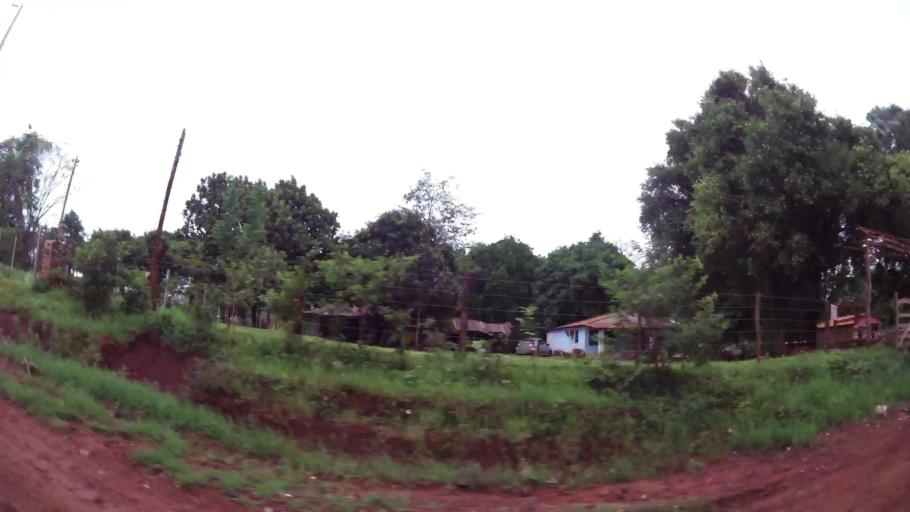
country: PY
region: Alto Parana
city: Presidente Franco
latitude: -25.5465
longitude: -54.6535
